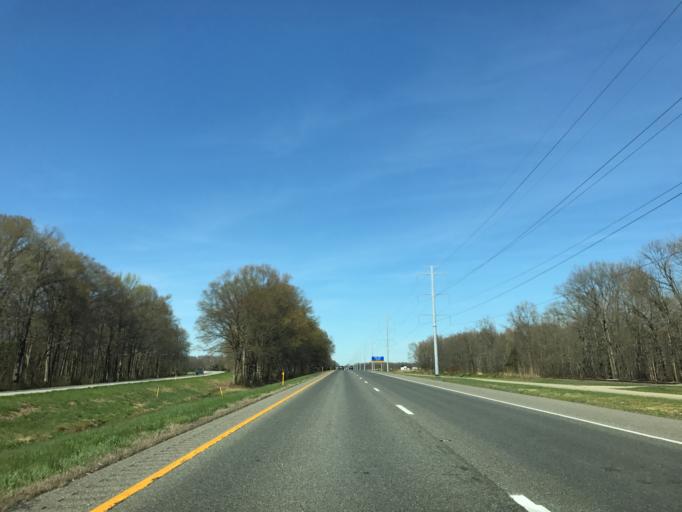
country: US
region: Maryland
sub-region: Queen Anne's County
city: Centreville
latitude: 39.0717
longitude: -75.9844
